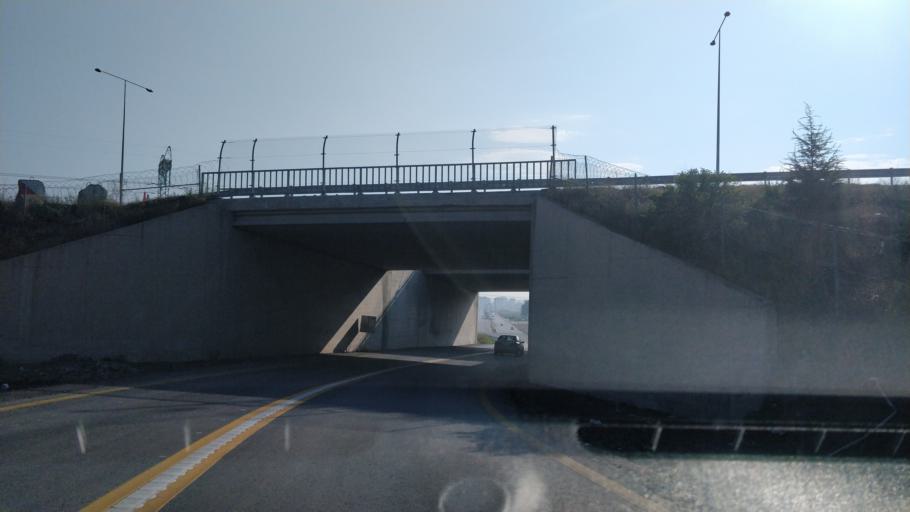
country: TR
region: Ankara
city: Etimesgut
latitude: 39.8853
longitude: 32.6114
